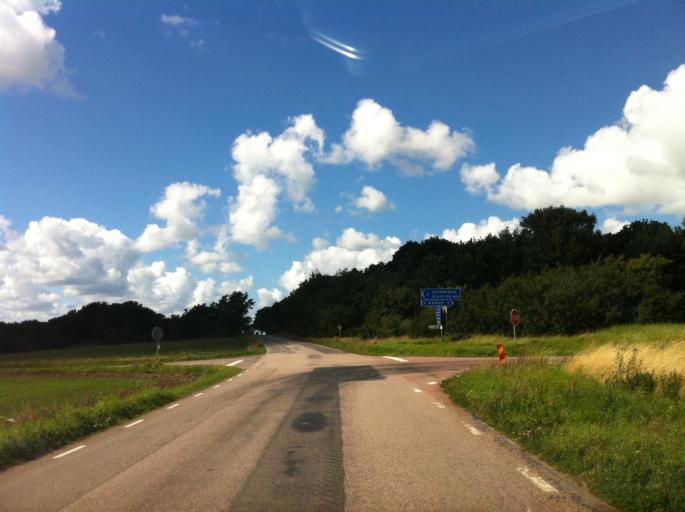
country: SE
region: Skane
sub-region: Angelholms Kommun
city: AEngelholm
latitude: 56.2506
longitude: 12.8755
